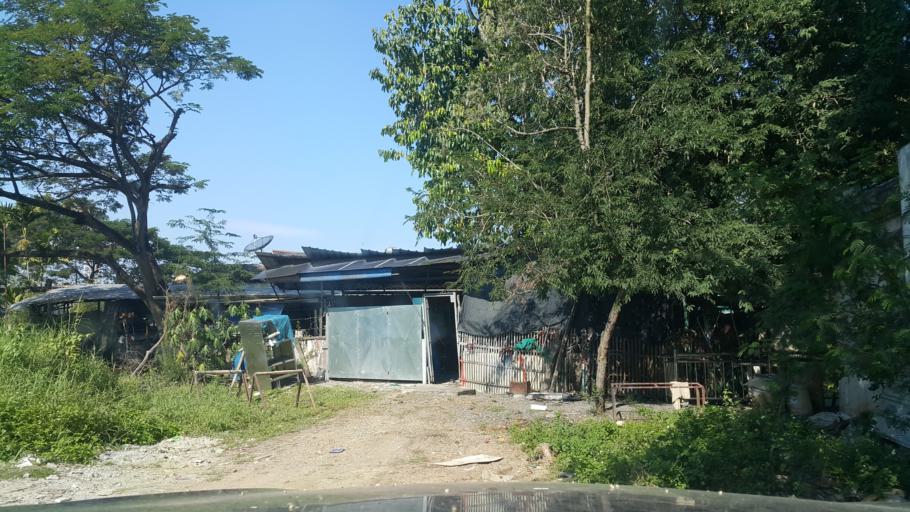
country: TH
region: Chiang Mai
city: Chiang Mai
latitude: 18.7737
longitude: 99.0364
